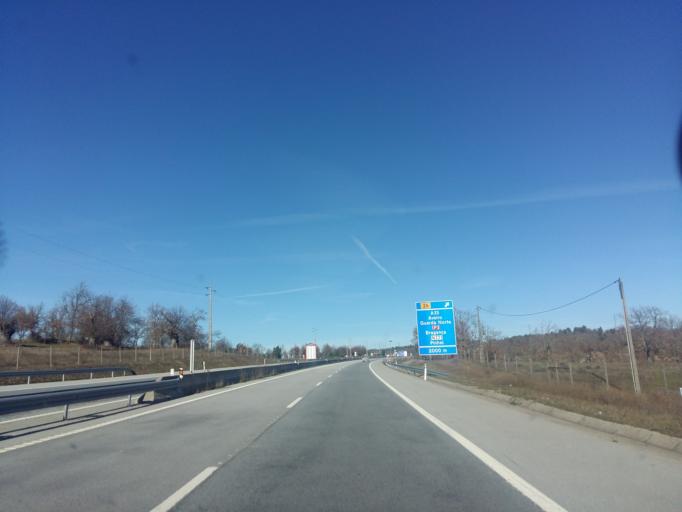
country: PT
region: Guarda
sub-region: Guarda
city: Sequeira
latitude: 40.5371
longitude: -7.2175
